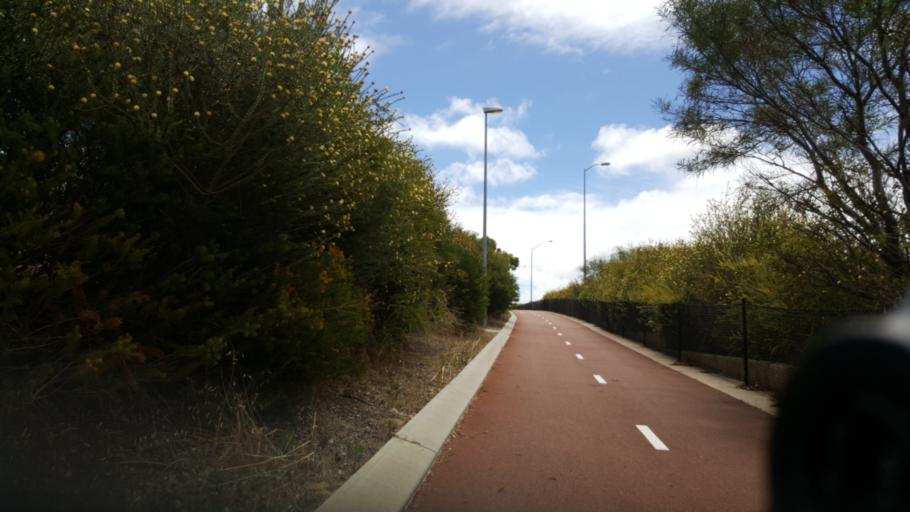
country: AU
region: Western Australia
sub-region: Stirling
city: Westminster
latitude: -31.8675
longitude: 115.8736
